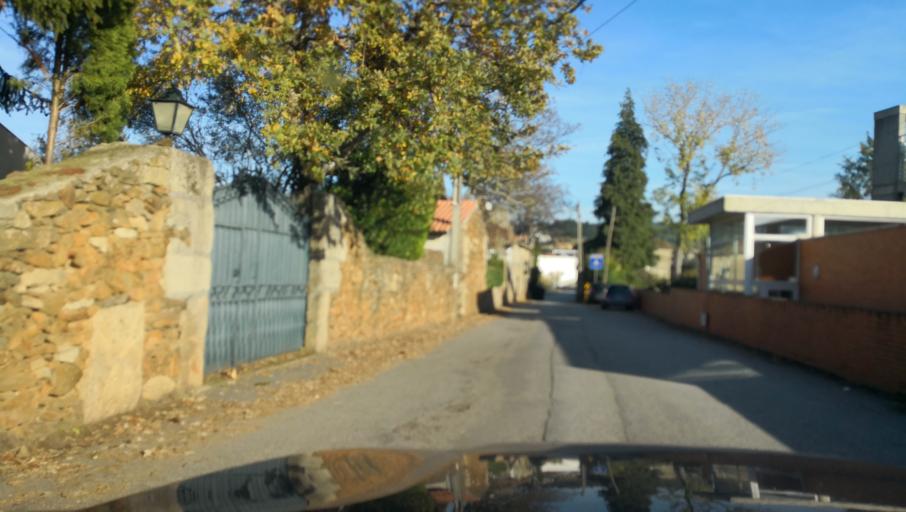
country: PT
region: Vila Real
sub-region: Vila Real
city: Vila Real
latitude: 41.3001
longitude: -7.7195
